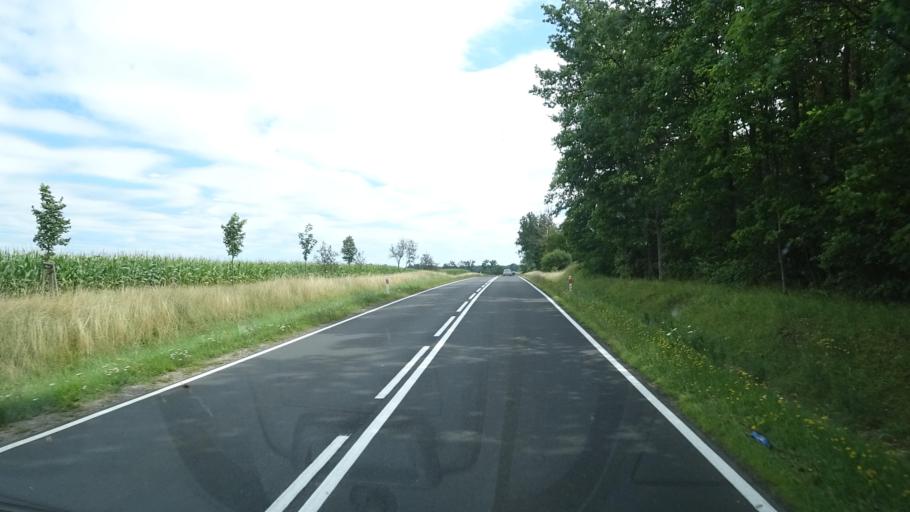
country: PL
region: Warmian-Masurian Voivodeship
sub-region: Powiat elcki
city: Stare Juchy
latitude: 53.7915
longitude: 22.1918
